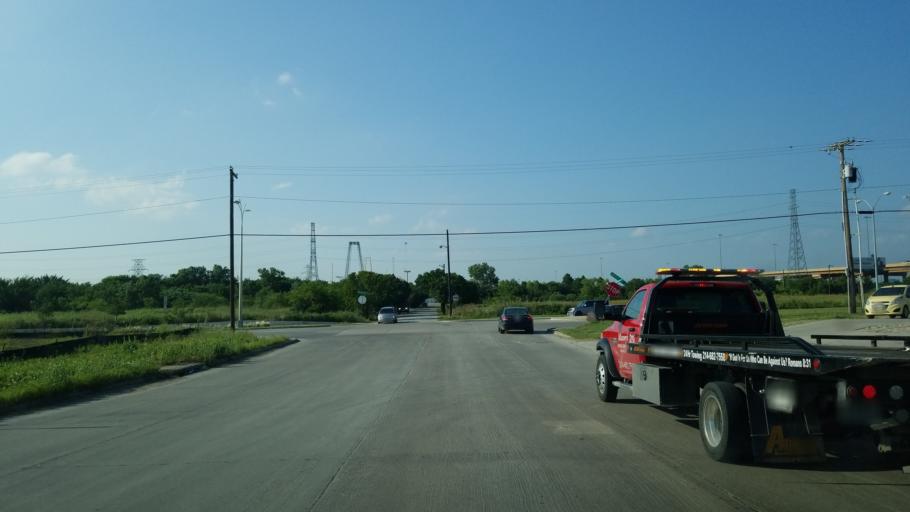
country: US
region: Texas
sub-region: Dallas County
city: Farmers Branch
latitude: 32.8805
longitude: -96.9005
